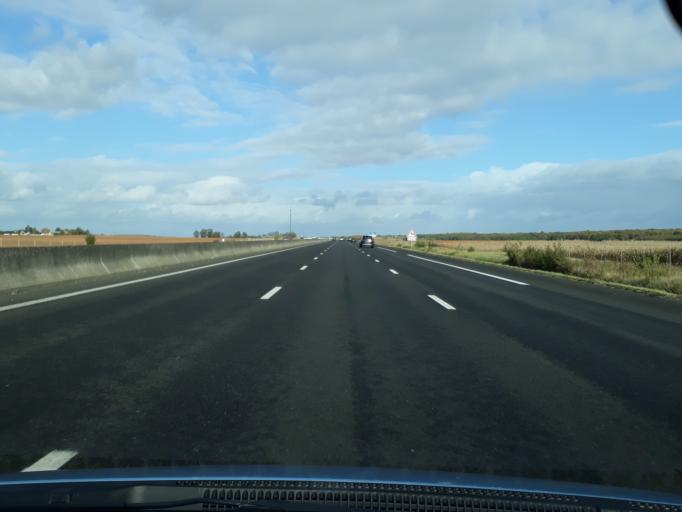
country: FR
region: Centre
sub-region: Departement du Loir-et-Cher
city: La Chaussee-Saint-Victor
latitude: 47.6492
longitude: 1.3713
